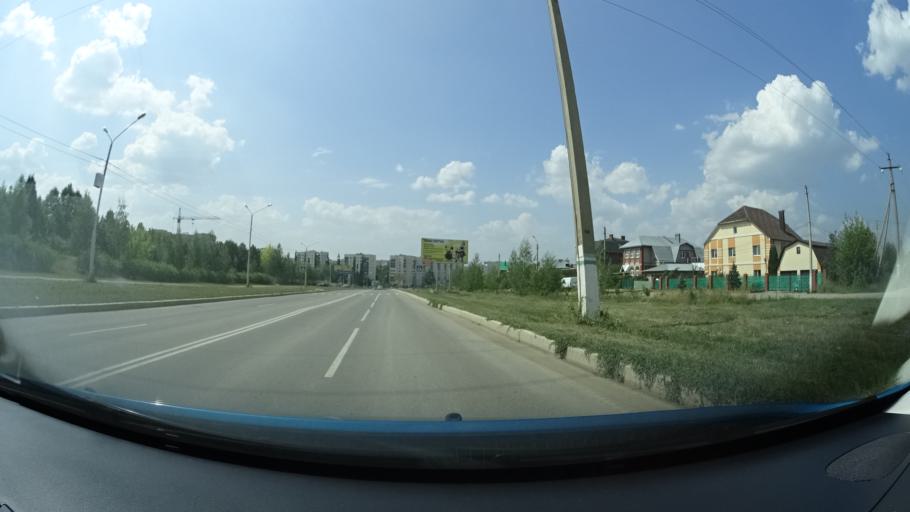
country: RU
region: Bashkortostan
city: Oktyabr'skiy
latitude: 54.4818
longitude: 53.5349
